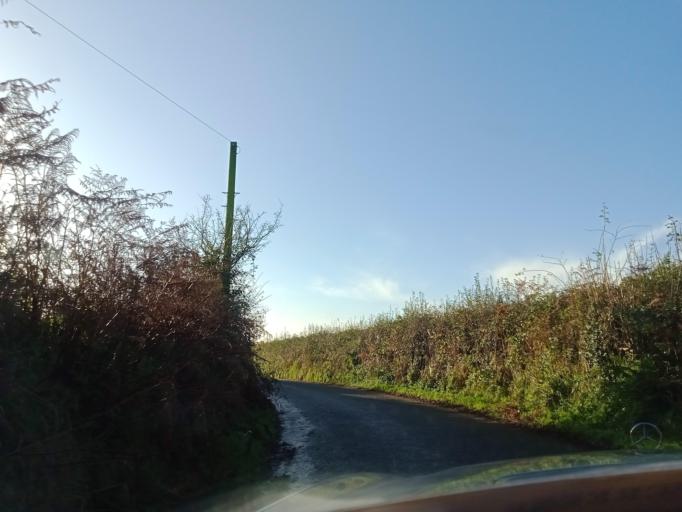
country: IE
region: Leinster
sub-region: Kilkenny
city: Mooncoin
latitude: 52.2881
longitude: -7.1933
